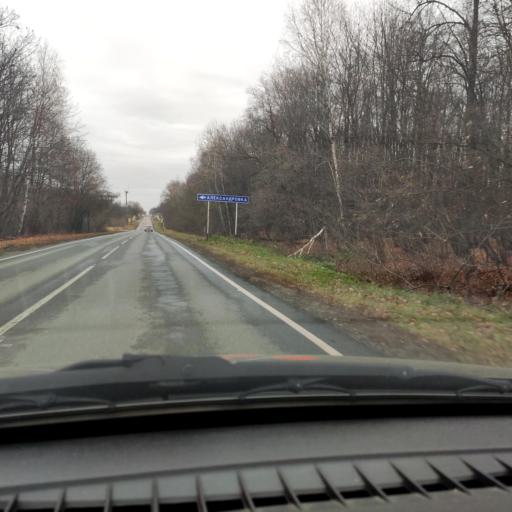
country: RU
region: Samara
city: Zhigulevsk
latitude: 53.3410
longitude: 49.4598
